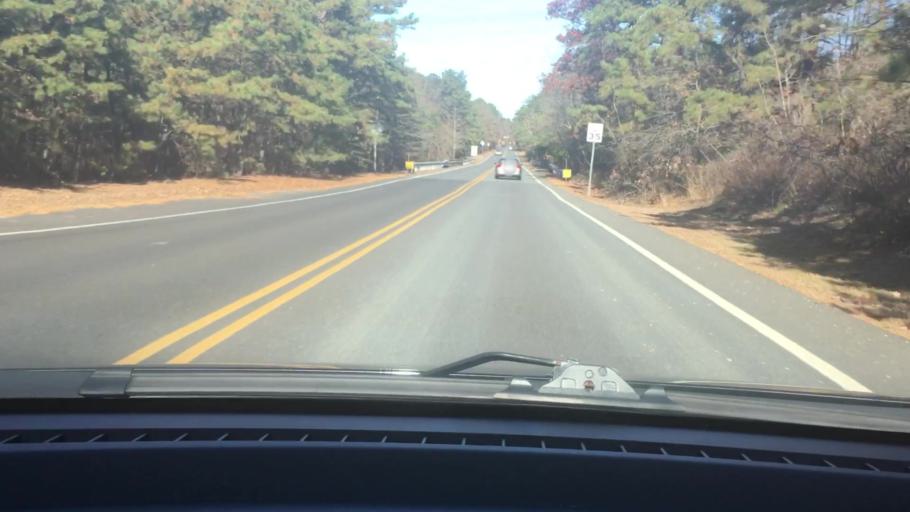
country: US
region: New Jersey
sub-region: Ocean County
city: Leisure Village East
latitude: 40.0113
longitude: -74.1610
